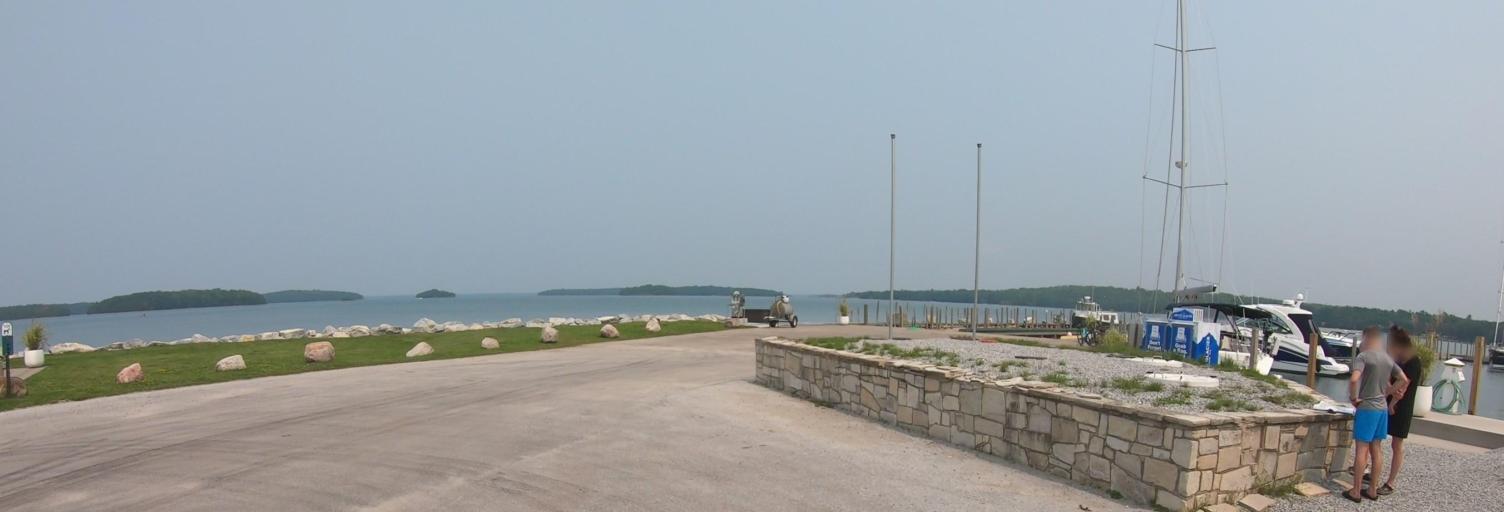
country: CA
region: Ontario
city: Thessalon
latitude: 46.0254
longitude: -83.7496
